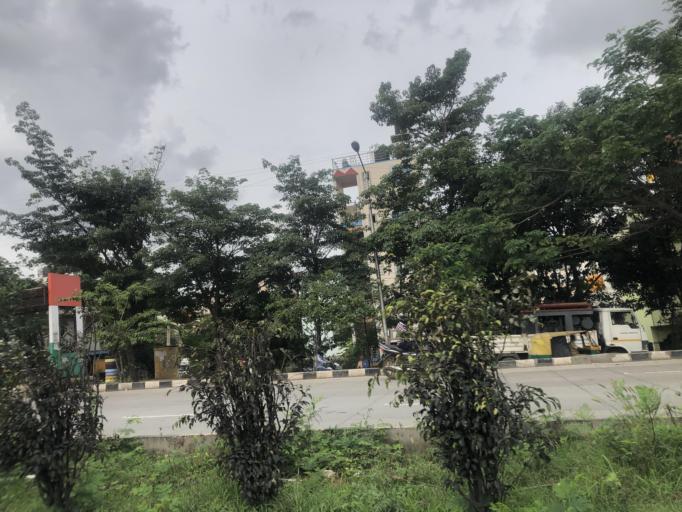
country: IN
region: Karnataka
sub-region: Bangalore Urban
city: Bangalore
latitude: 12.9680
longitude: 77.5126
